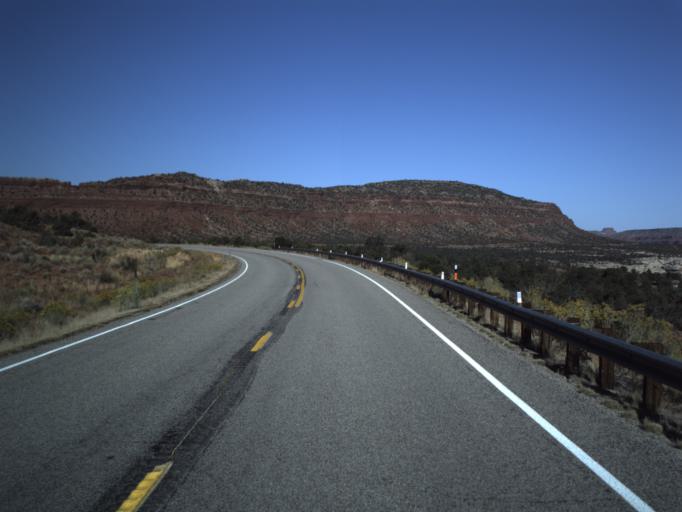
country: US
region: Utah
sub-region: San Juan County
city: Blanding
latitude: 37.6040
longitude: -110.0634
